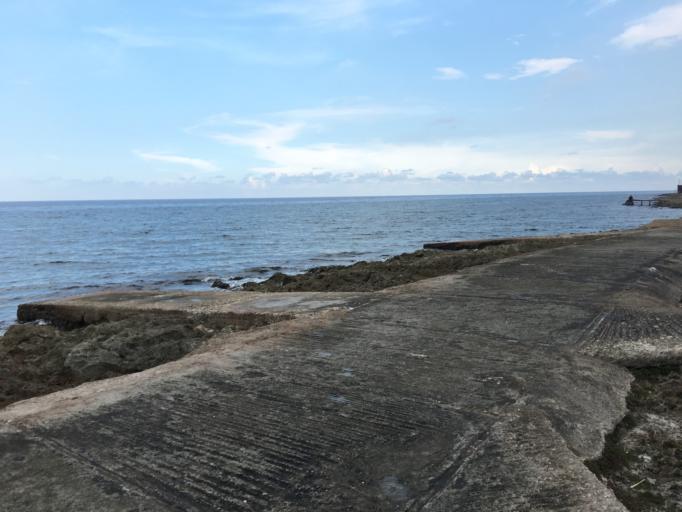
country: CU
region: La Habana
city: Havana
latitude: 23.1144
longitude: -82.4392
